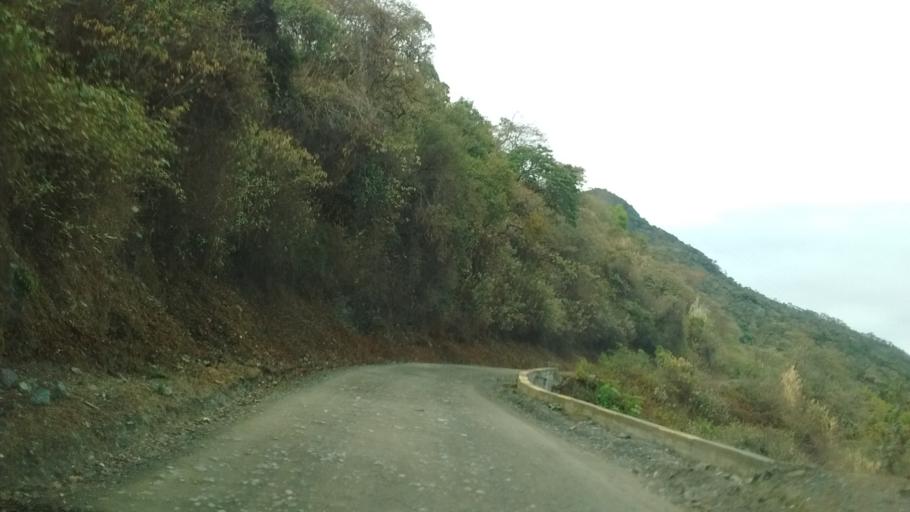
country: CO
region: Cauca
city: Almaguer
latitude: 1.8607
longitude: -76.9343
